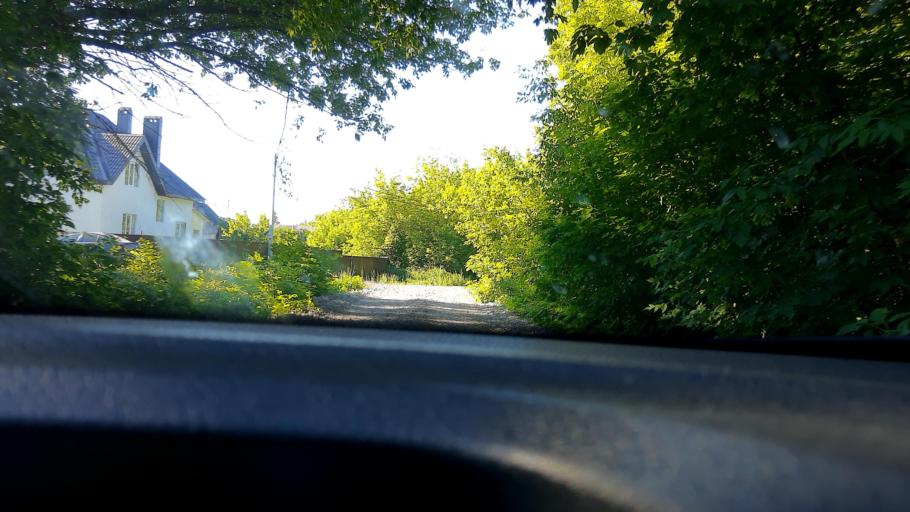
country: RU
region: Bashkortostan
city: Avdon
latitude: 54.6517
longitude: 55.7681
